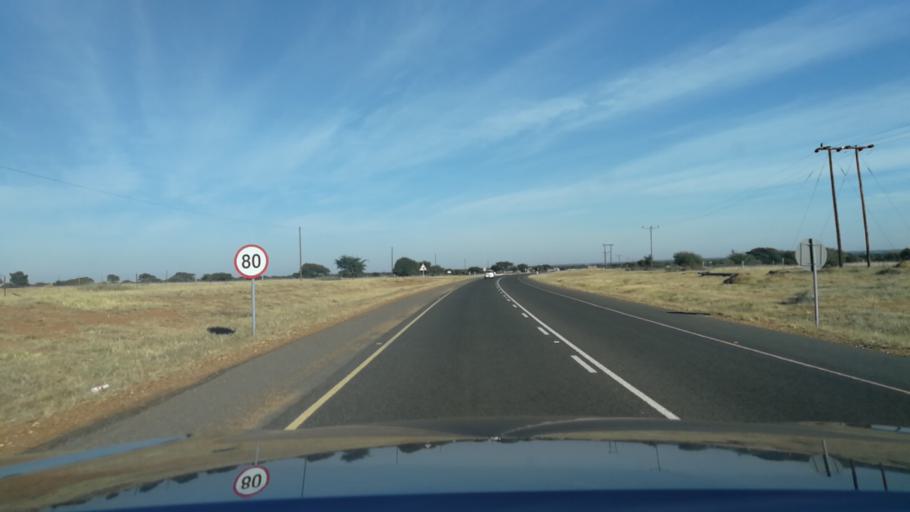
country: BW
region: South East
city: Janeng
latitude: -25.4782
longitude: 25.5119
